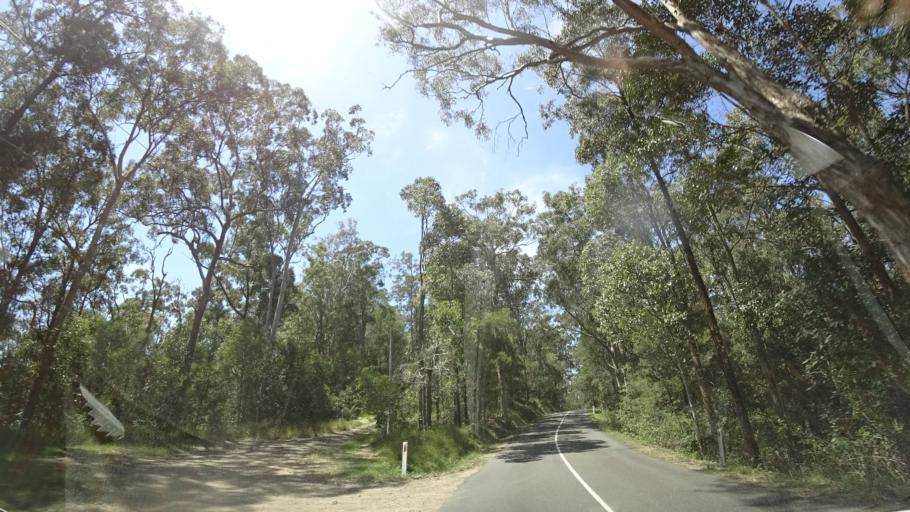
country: AU
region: Queensland
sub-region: Moreton Bay
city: Highvale
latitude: -27.4045
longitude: 152.8156
